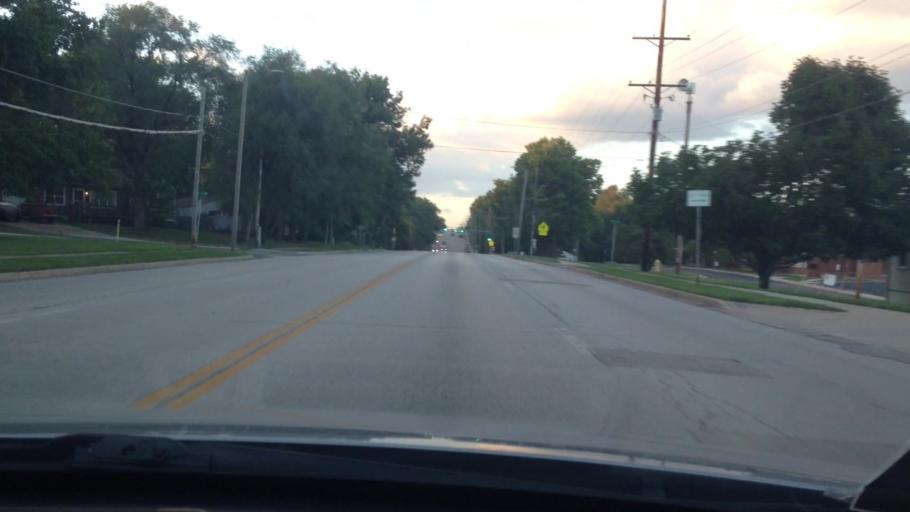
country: US
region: Missouri
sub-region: Jackson County
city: Raytown
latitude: 38.9751
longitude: -94.4649
